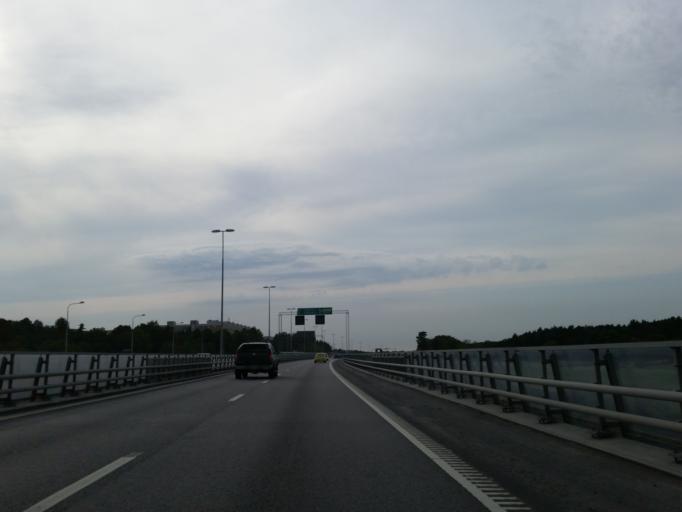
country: SE
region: Stockholm
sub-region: Stockholms Kommun
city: Kista
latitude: 59.3941
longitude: 17.9231
